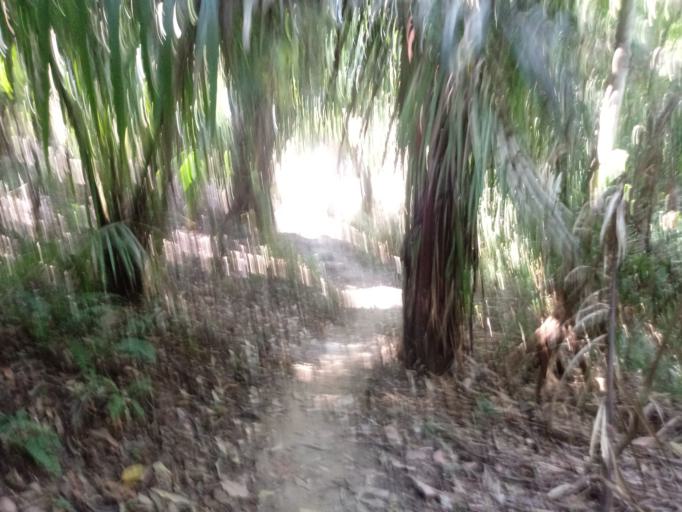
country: CR
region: Puntarenas
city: Paquera
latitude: 9.5862
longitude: -85.0981
